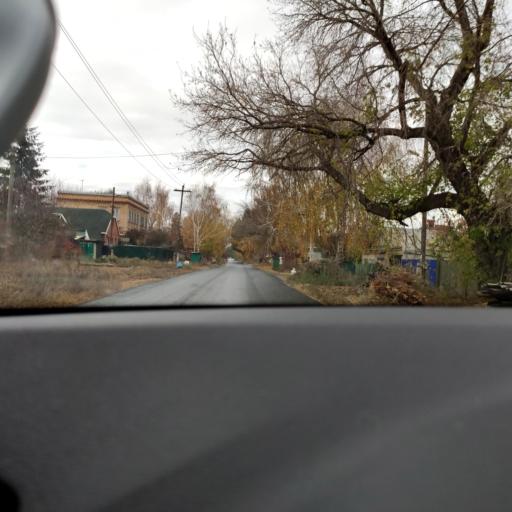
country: RU
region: Samara
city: Smyshlyayevka
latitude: 53.2442
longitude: 50.3277
